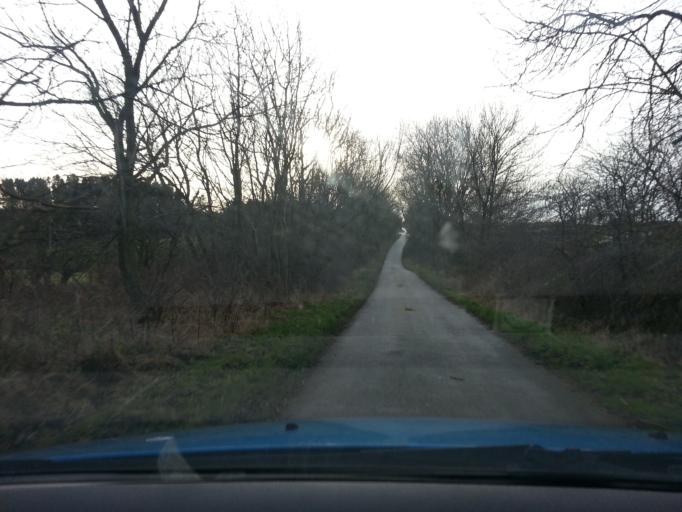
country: GB
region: England
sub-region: County Durham
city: Tow Law
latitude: 54.7256
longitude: -1.7783
